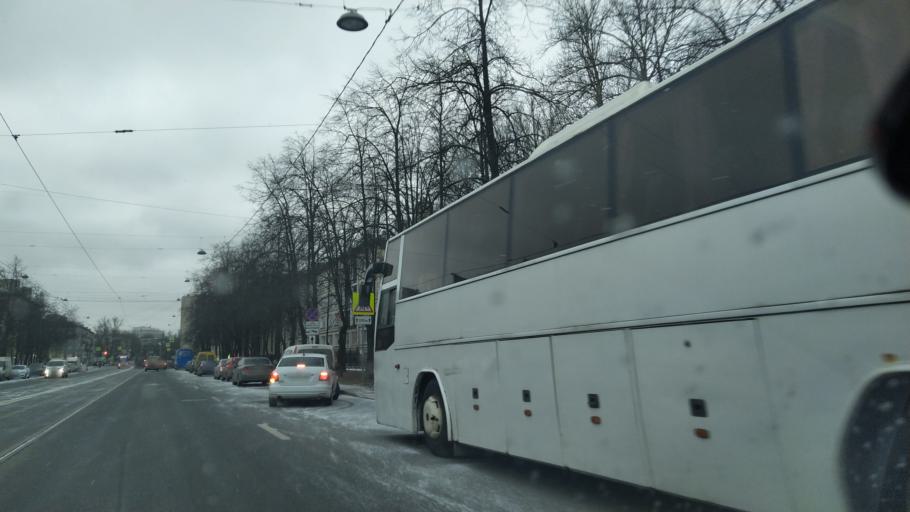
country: RU
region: St.-Petersburg
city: Kupchino
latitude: 59.8467
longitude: 30.3300
